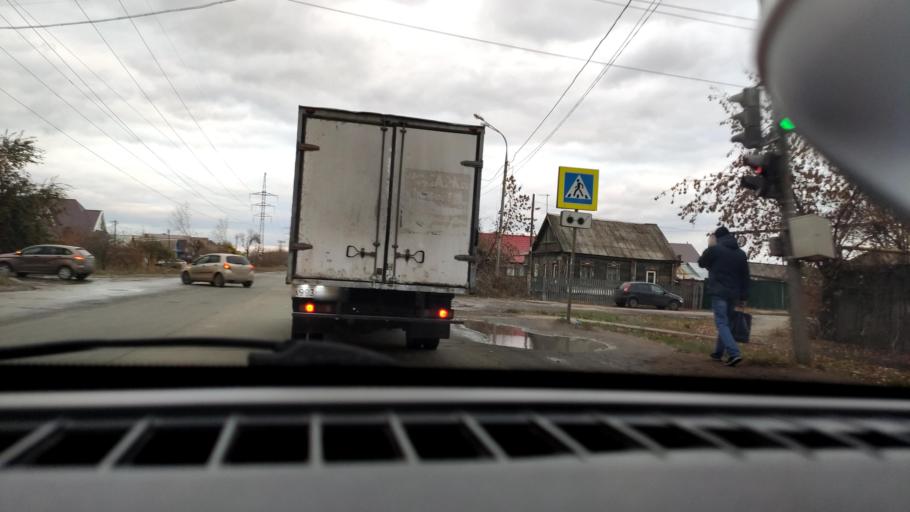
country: RU
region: Samara
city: Samara
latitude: 53.1337
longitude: 50.1241
